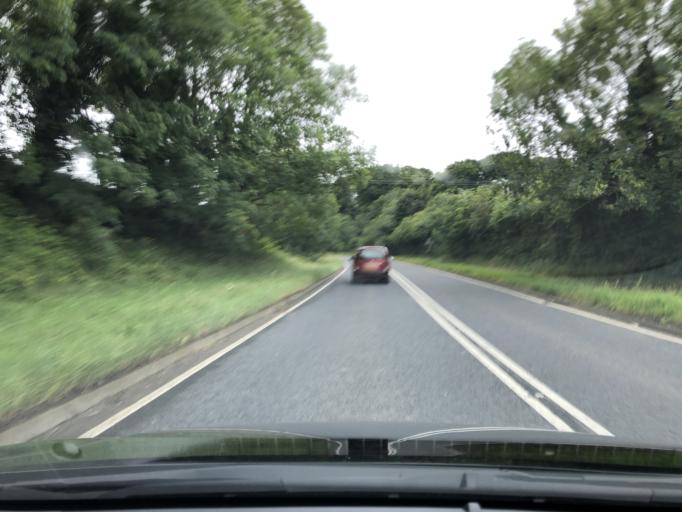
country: GB
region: Northern Ireland
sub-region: Down District
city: Dundrum
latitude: 54.3241
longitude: -5.8360
